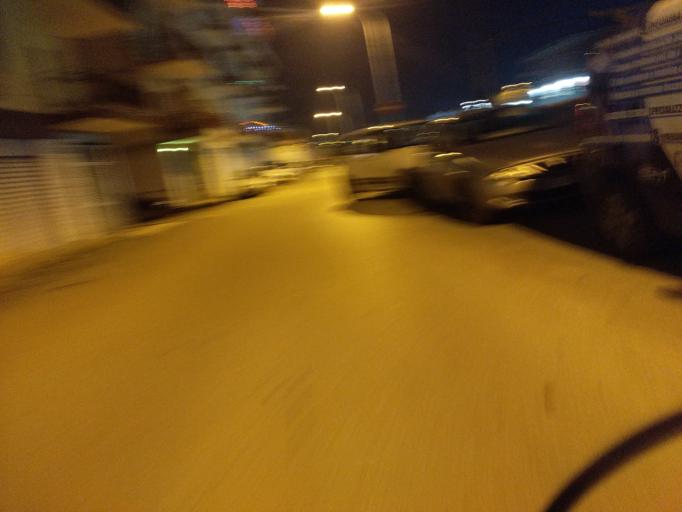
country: IT
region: Apulia
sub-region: Provincia di Bari
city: Modugno
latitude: 41.0868
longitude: 16.7803
